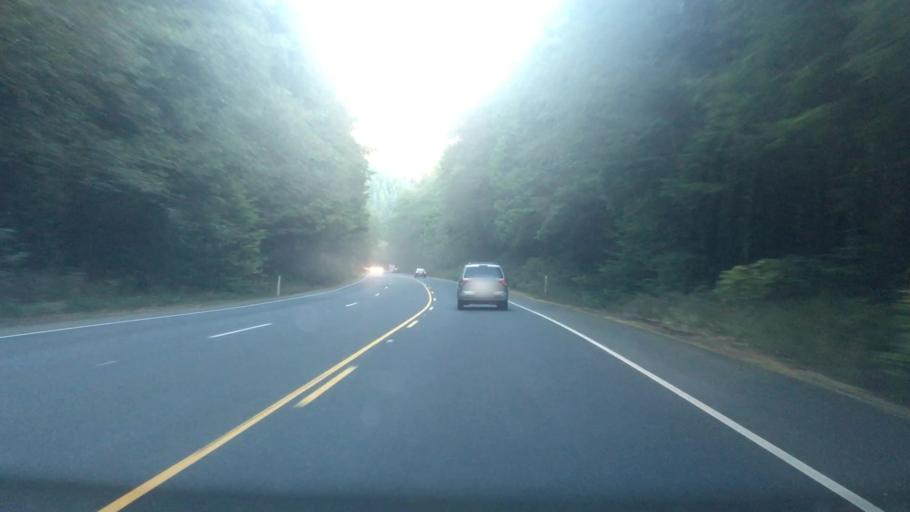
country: US
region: Oregon
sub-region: Clatsop County
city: Cannon Beach
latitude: 45.7786
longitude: -123.9522
